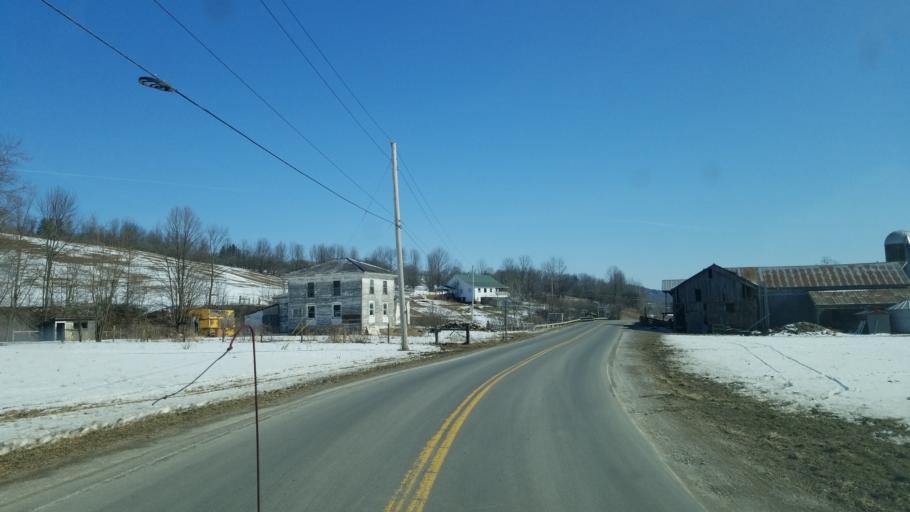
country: US
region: Pennsylvania
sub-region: Tioga County
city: Elkland
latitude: 42.0752
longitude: -77.4297
